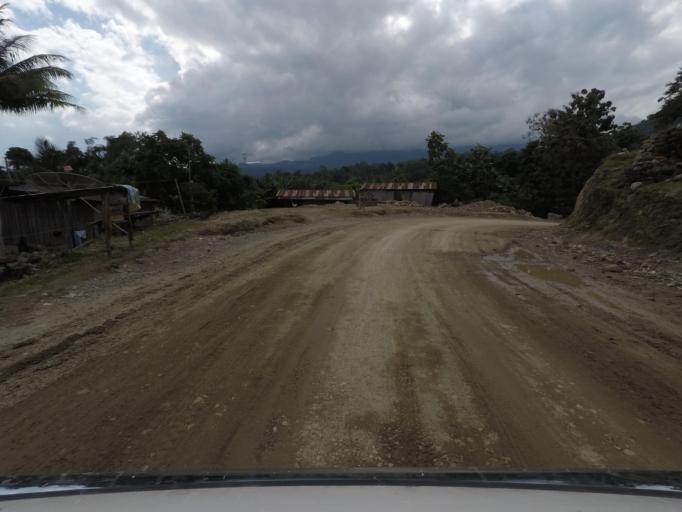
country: TL
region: Viqueque
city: Viqueque
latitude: -8.7815
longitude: 126.3756
